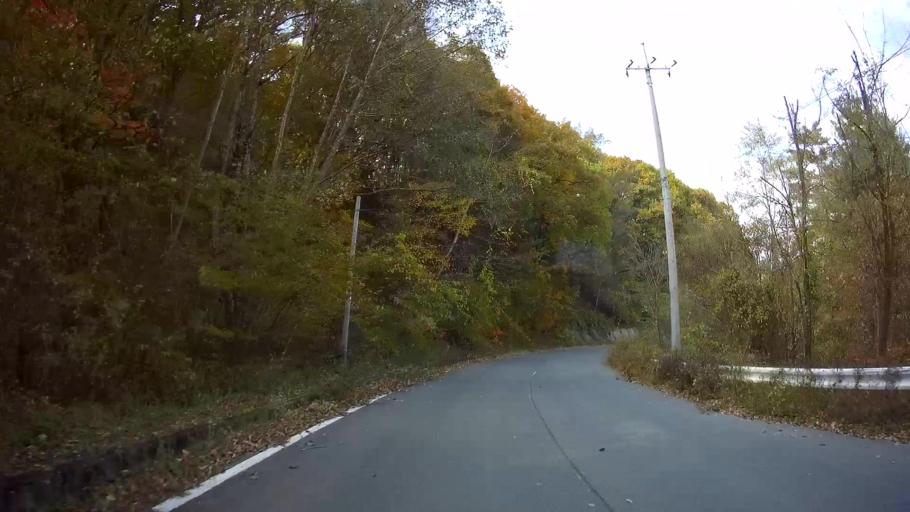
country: JP
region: Gunma
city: Nakanojomachi
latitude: 36.5366
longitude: 138.6558
